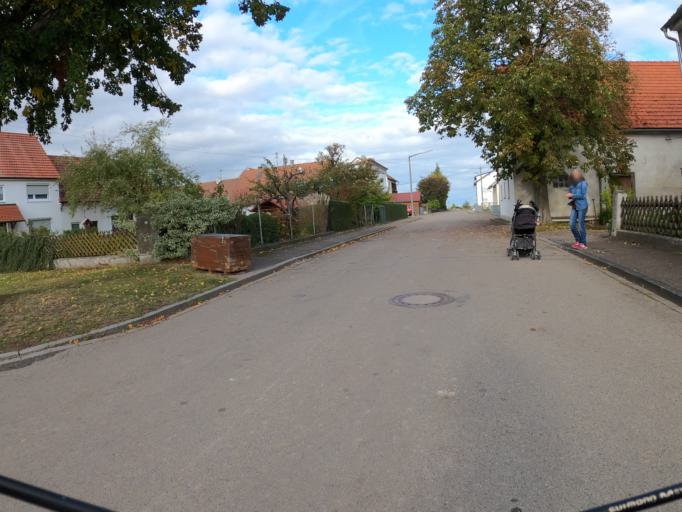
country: DE
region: Bavaria
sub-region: Swabia
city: Holzheim
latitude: 48.4007
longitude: 10.1059
